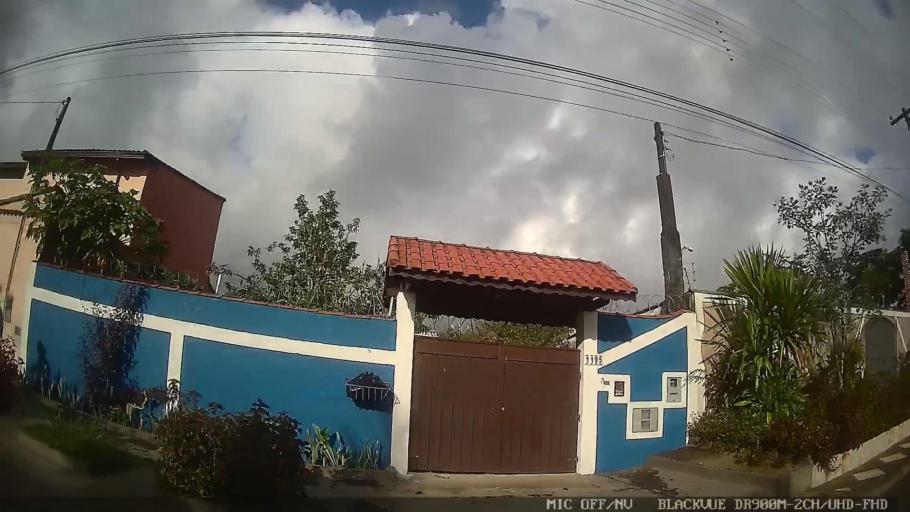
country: BR
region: Sao Paulo
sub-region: Itanhaem
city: Itanhaem
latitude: -24.1913
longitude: -46.8631
